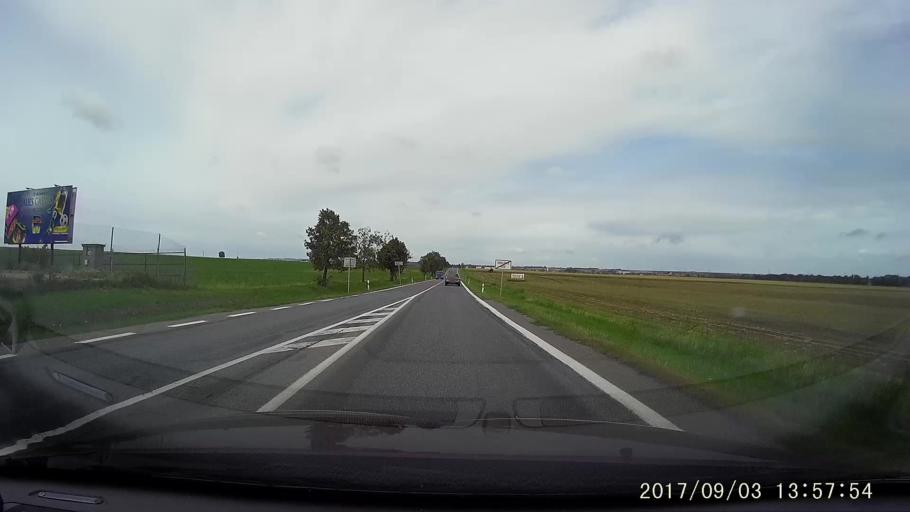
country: CZ
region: South Moravian
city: Vrbovec
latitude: 48.7699
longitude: 16.0703
